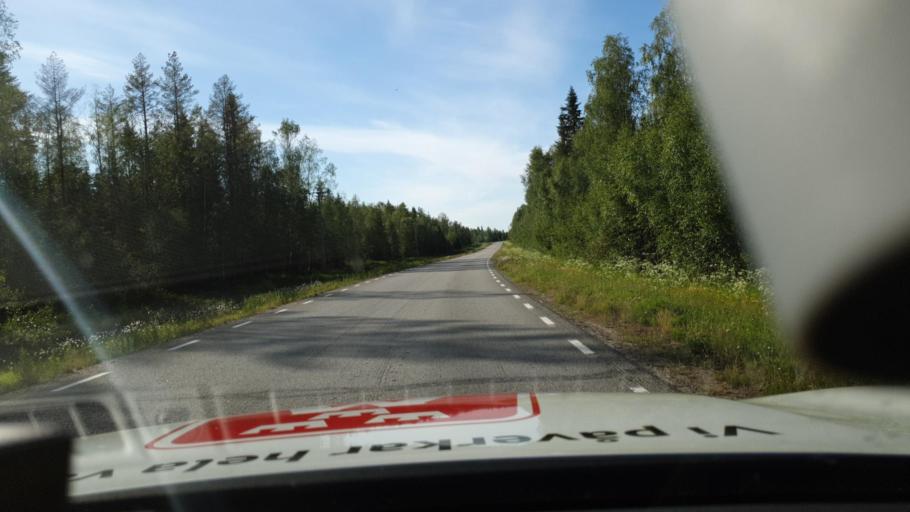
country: SE
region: Norrbotten
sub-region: Kalix Kommun
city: Toere
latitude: 65.8975
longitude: 22.6223
